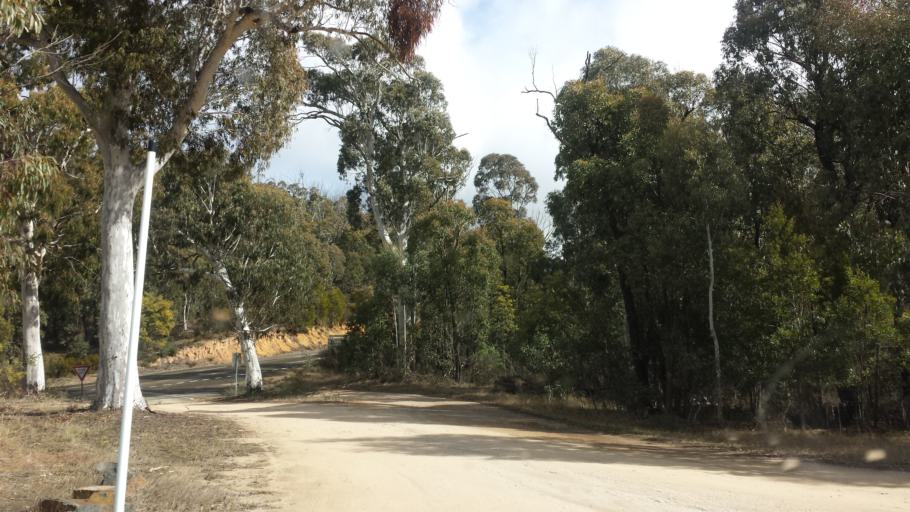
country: AU
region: Victoria
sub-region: Alpine
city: Mount Beauty
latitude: -37.1270
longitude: 147.5344
